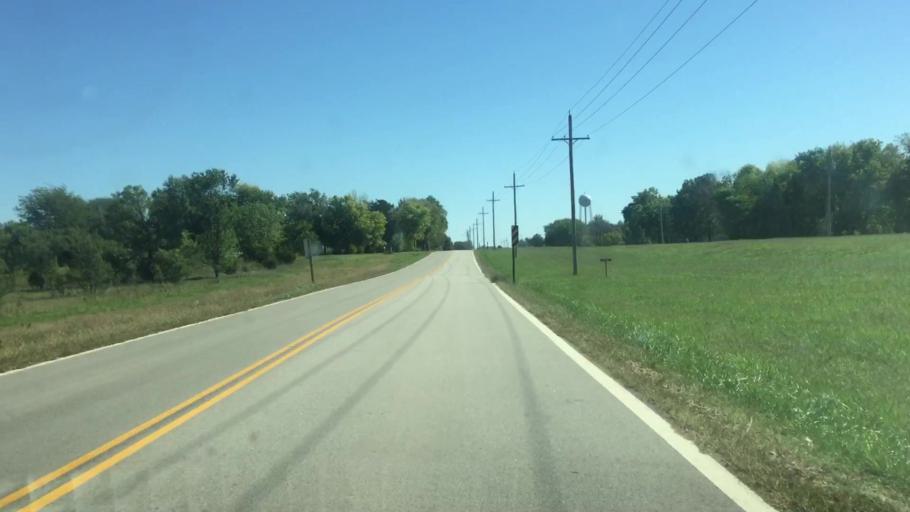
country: US
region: Kansas
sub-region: Jackson County
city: Holton
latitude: 39.6069
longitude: -95.7218
